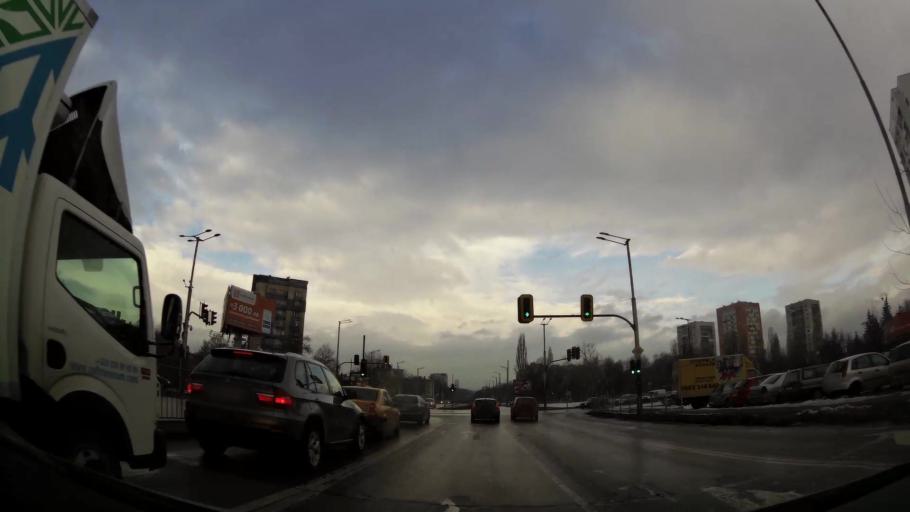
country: BG
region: Sofia-Capital
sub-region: Stolichna Obshtina
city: Sofia
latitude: 42.7059
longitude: 23.2853
